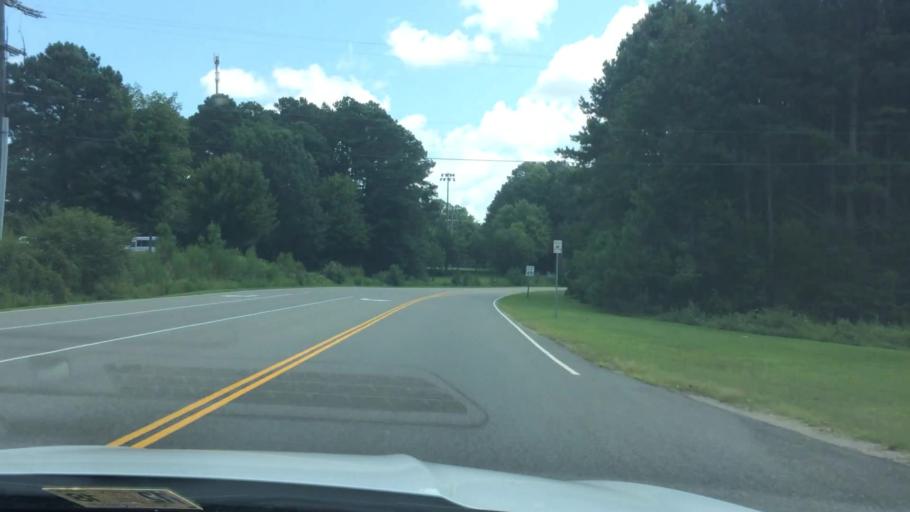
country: US
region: Virginia
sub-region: James City County
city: Williamsburg
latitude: 37.2958
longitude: -76.7374
